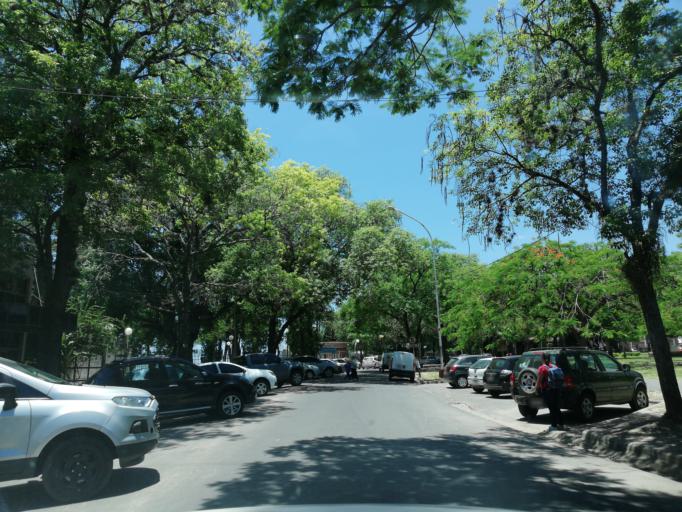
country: AR
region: Corrientes
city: Corrientes
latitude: -27.4589
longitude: -58.8294
